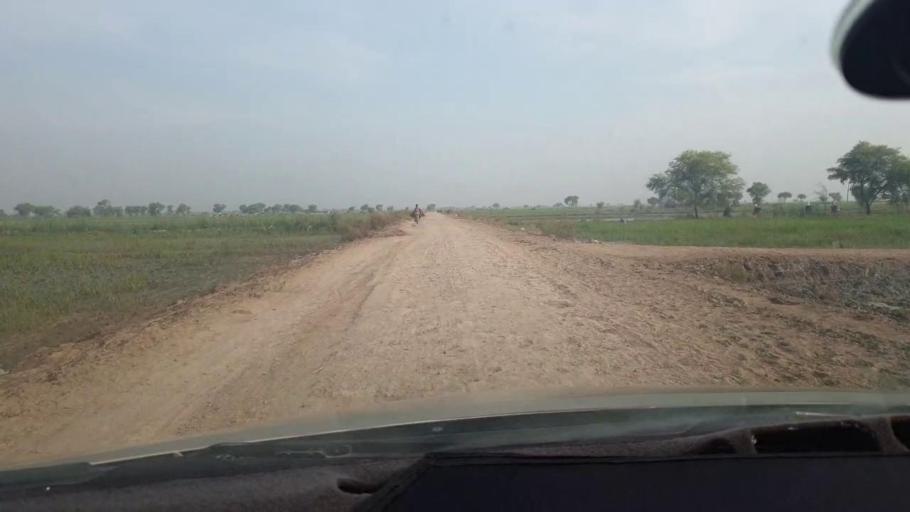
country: PK
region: Balochistan
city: Jhatpat
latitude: 28.3520
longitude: 68.4098
